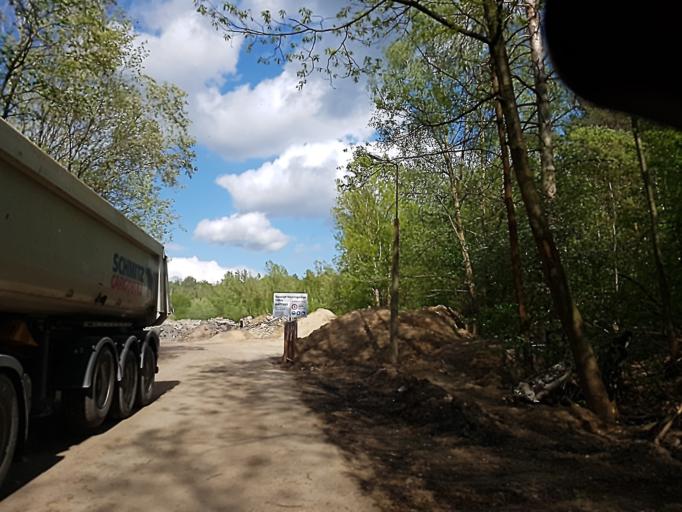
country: DE
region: Brandenburg
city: Trobitz
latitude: 51.5892
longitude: 13.4393
